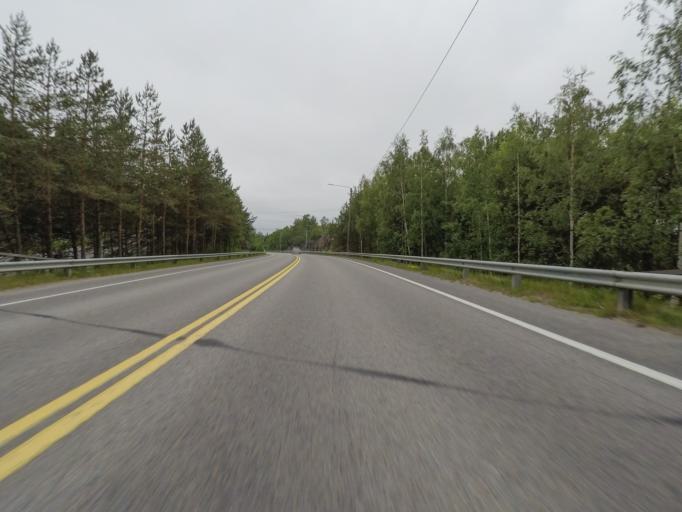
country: FI
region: Varsinais-Suomi
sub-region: Turku
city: Raisio
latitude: 60.4671
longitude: 22.1286
